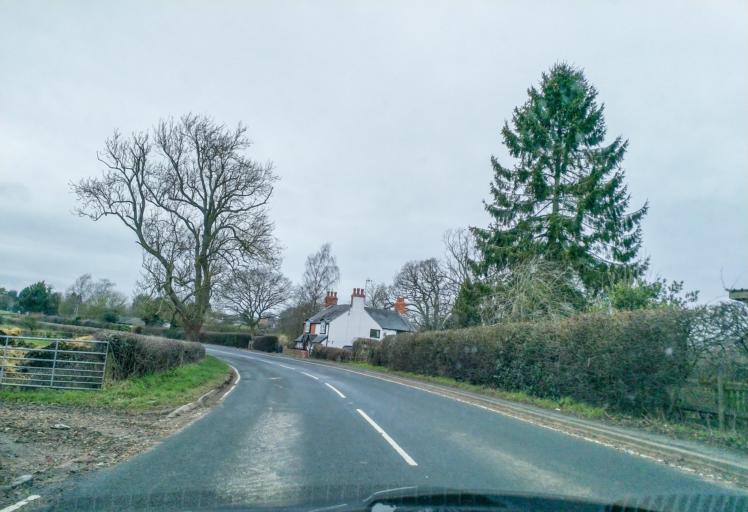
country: GB
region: England
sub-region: Warwickshire
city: Wroxall
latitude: 52.3022
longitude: -1.6664
